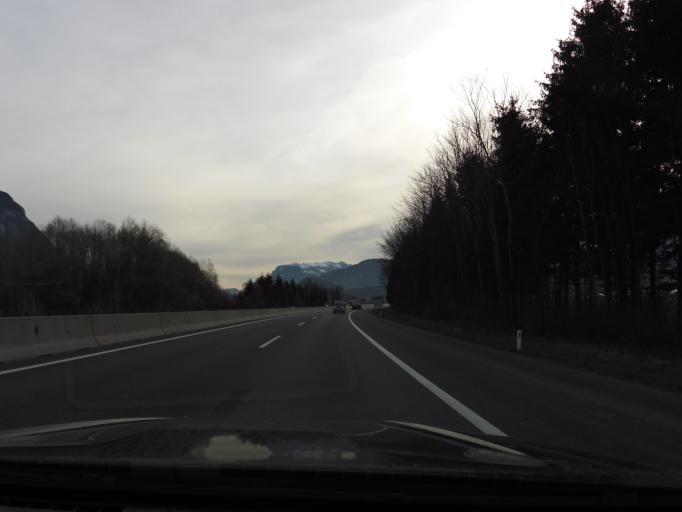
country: AT
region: Tyrol
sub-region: Politischer Bezirk Kufstein
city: Langkampfen
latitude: 47.5313
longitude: 12.0826
